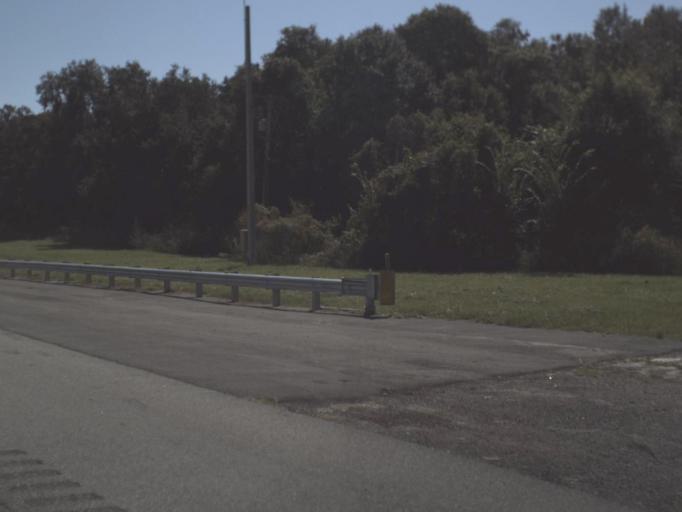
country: US
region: Florida
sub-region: Sumter County
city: Wildwood
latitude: 28.8291
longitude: -82.0318
